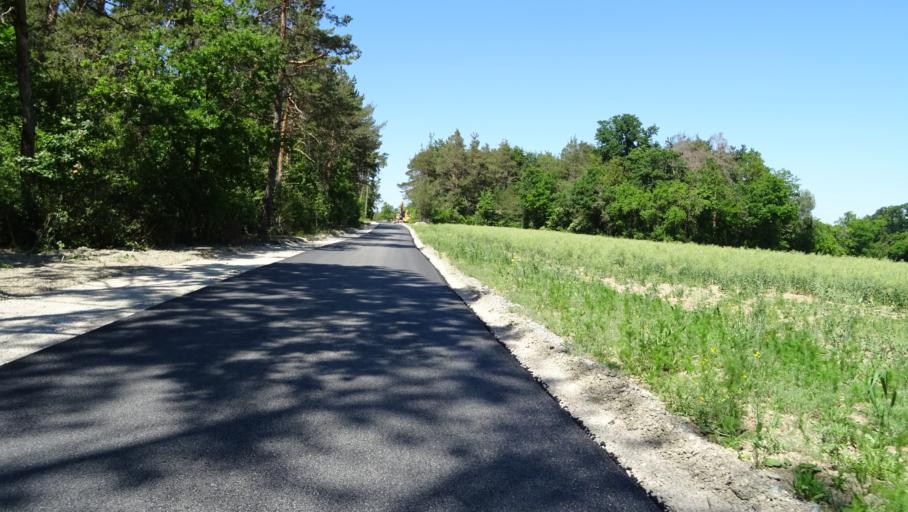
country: DE
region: Baden-Wuerttemberg
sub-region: Karlsruhe Region
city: Buchen
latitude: 49.4861
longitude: 9.3288
